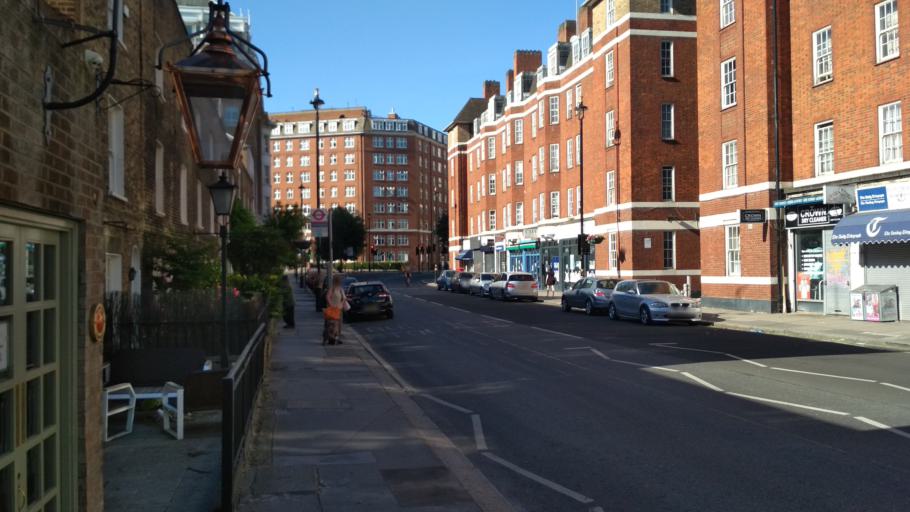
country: GB
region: England
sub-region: Greater London
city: Battersea
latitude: 51.4897
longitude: -0.1503
